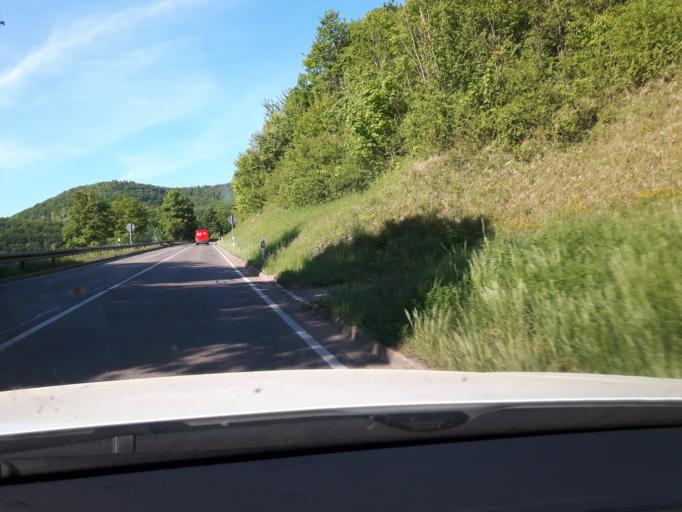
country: DE
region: Baden-Wuerttemberg
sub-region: Tuebingen Region
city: Pfullingen
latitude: 48.4371
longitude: 9.2612
